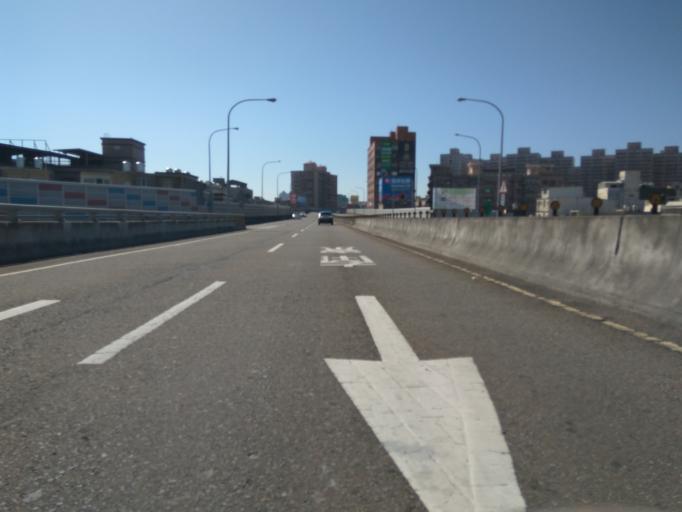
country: TW
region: Taiwan
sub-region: Hsinchu
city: Hsinchu
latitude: 24.8259
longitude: 120.9717
